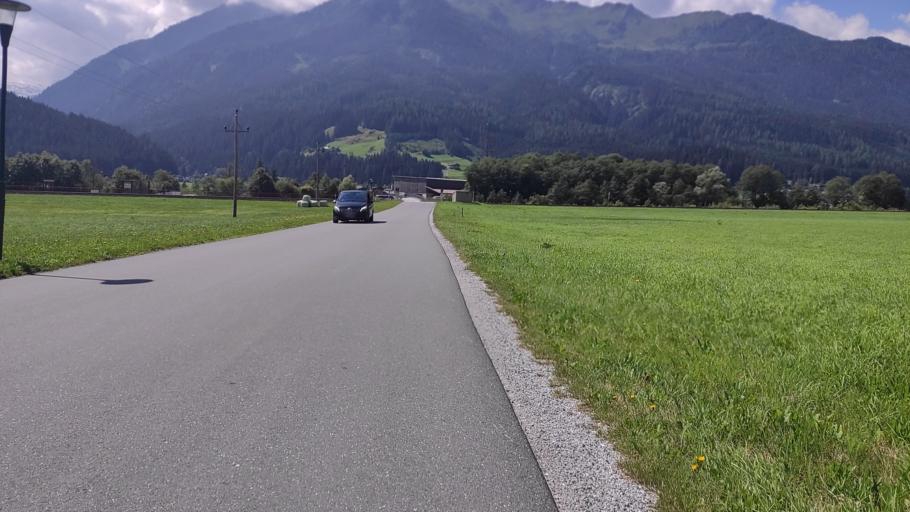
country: AT
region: Salzburg
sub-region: Politischer Bezirk Zell am See
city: Bramberg am Wildkogel
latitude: 47.2583
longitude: 12.3179
